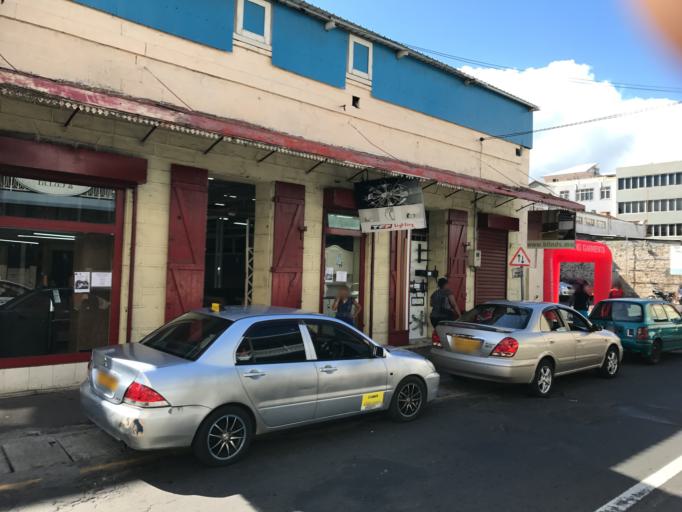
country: MU
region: Port Louis
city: Port Louis
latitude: -20.1598
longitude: 57.5038
